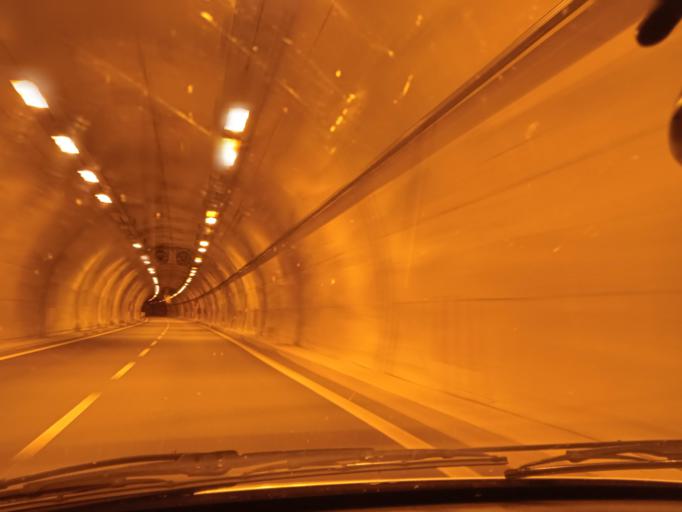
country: IT
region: Sicily
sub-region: Messina
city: Caronia
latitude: 38.0191
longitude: 14.4387
